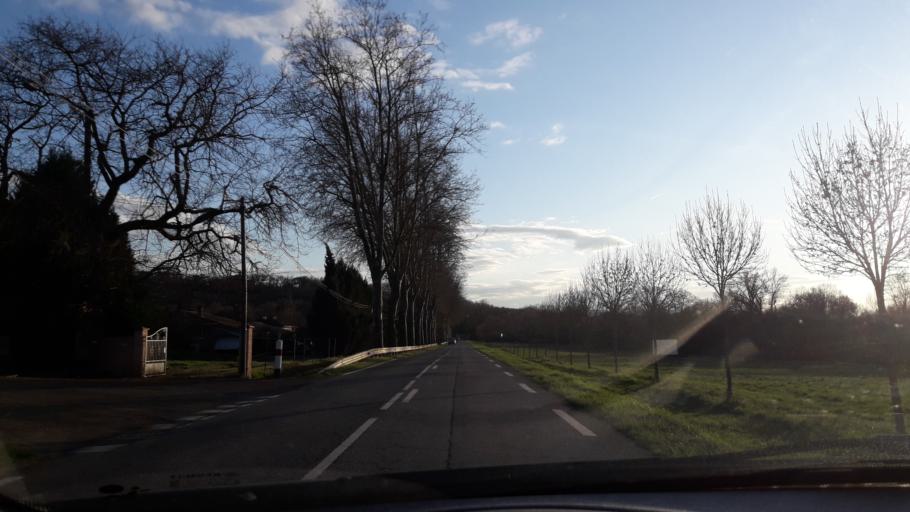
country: FR
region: Midi-Pyrenees
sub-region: Departement de la Haute-Garonne
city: Montaigut-sur-Save
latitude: 43.6987
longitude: 1.2378
